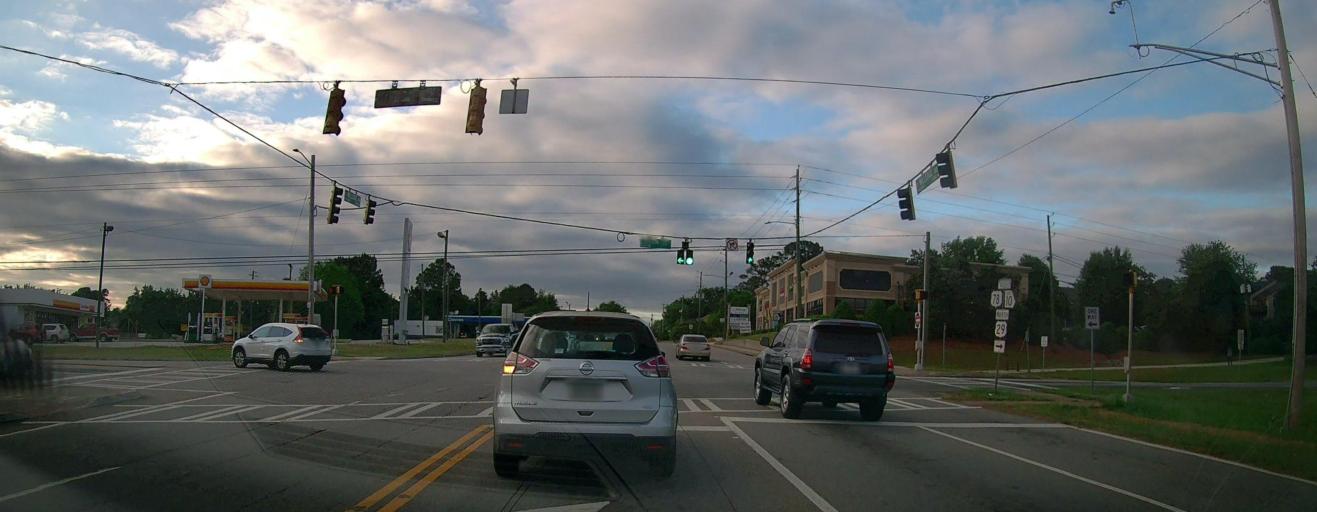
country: US
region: Georgia
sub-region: Clarke County
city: Athens
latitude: 33.9219
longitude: -83.3783
